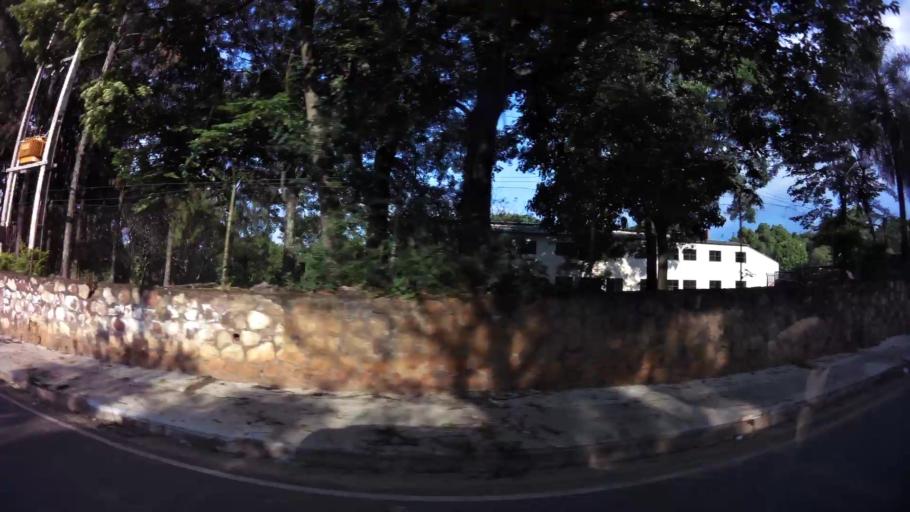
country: PY
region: Central
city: Fernando de la Mora
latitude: -25.3441
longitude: -57.5207
